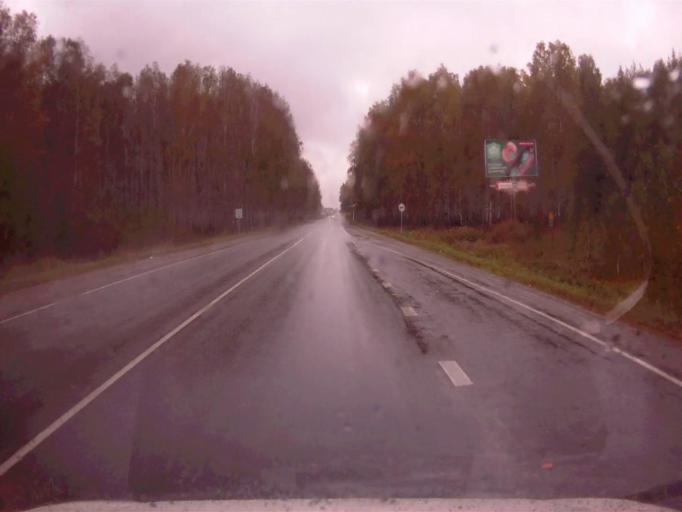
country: RU
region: Chelyabinsk
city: Argayash
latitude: 55.4133
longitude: 61.0361
